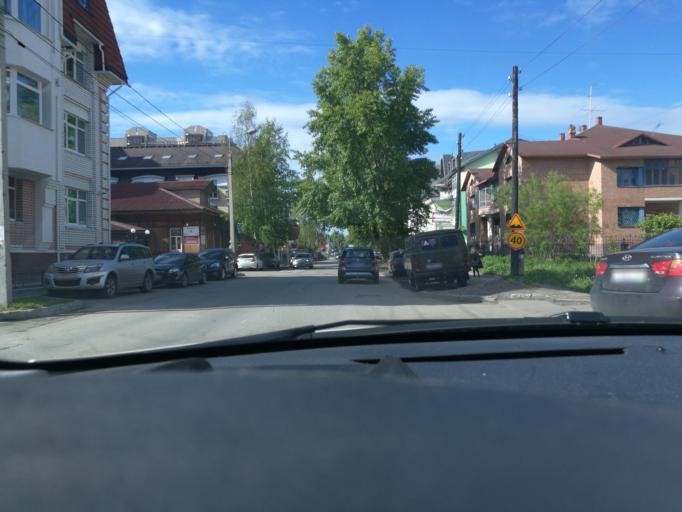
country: RU
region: Arkhangelskaya
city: Arkhangel'sk
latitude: 64.5385
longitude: 40.5313
